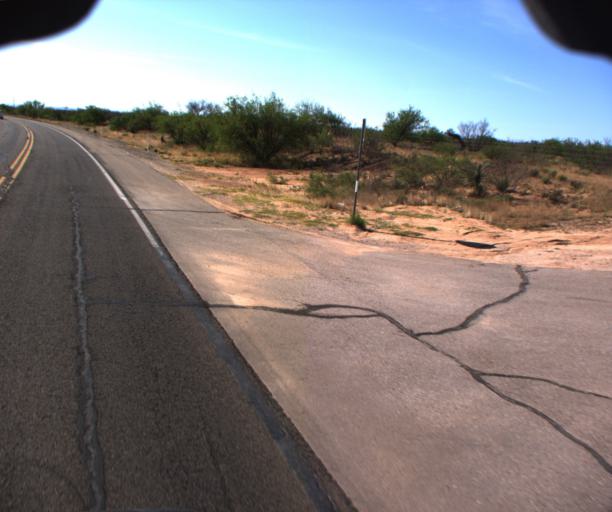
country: US
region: Arizona
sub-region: Cochise County
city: Benson
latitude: 31.9329
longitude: -110.2842
